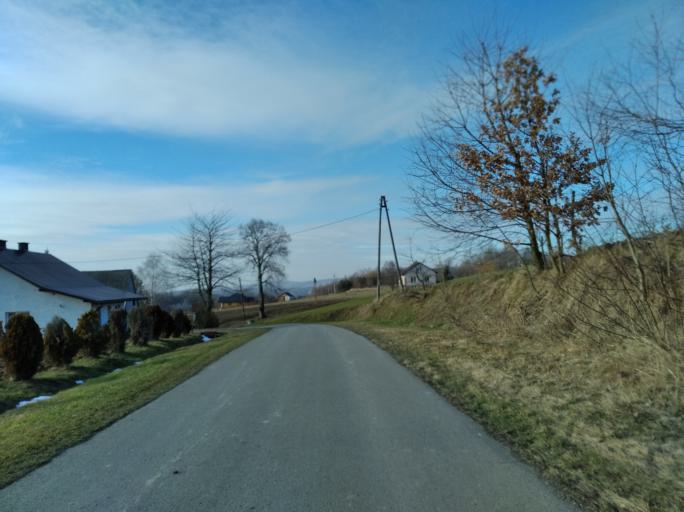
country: PL
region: Subcarpathian Voivodeship
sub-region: Powiat strzyzowski
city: Gwoznica Gorna
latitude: 49.8271
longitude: 21.9691
